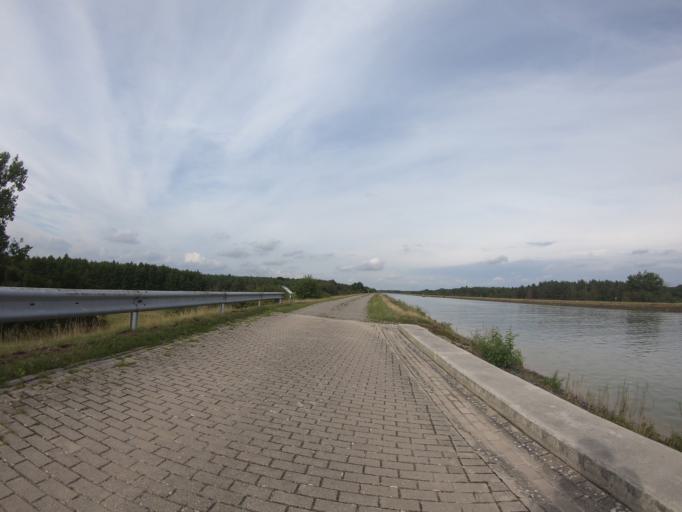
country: DE
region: Lower Saxony
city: Osloss
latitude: 52.4598
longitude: 10.6440
